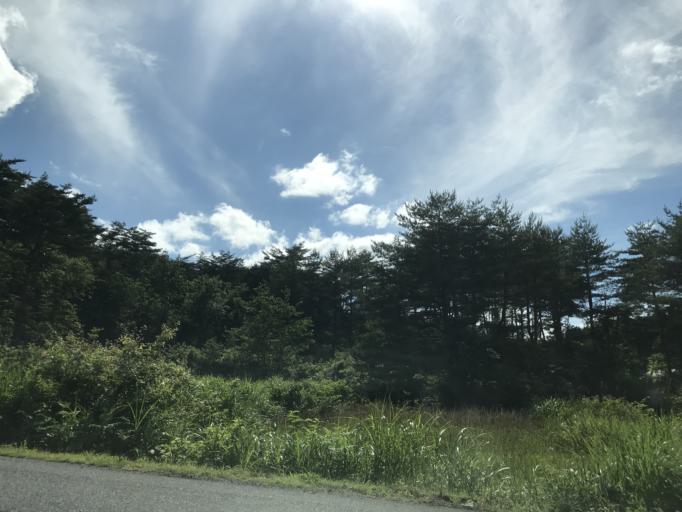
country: JP
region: Iwate
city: Ichinoseki
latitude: 38.9219
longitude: 140.9963
